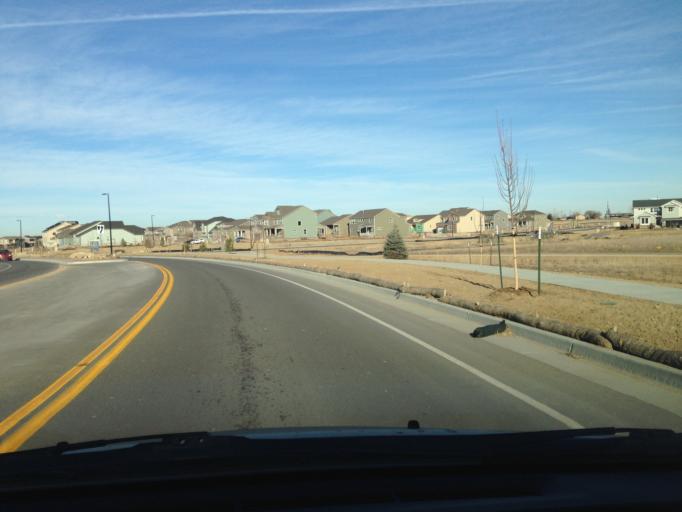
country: US
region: Colorado
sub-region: Boulder County
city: Lafayette
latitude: 40.0239
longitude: -105.0887
